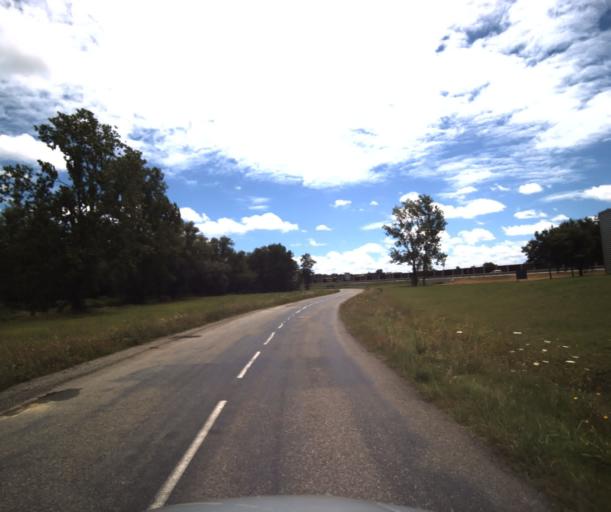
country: FR
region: Midi-Pyrenees
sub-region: Departement de la Haute-Garonne
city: Lacroix-Falgarde
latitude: 43.4838
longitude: 1.4031
